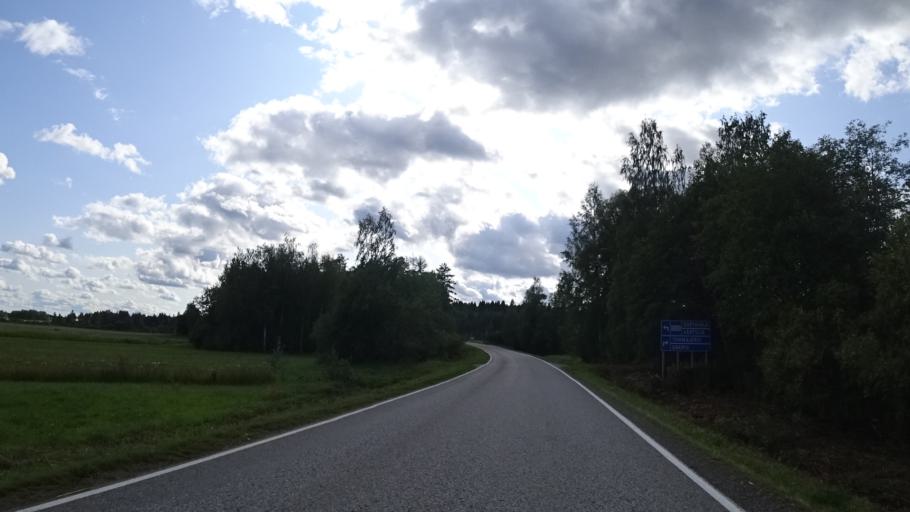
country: RU
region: Republic of Karelia
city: Vyartsilya
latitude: 62.2167
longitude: 30.6056
